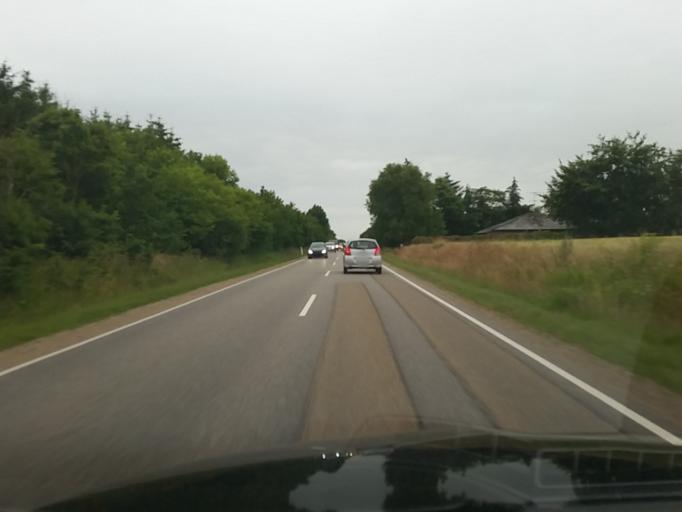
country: DK
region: South Denmark
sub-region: Billund Kommune
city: Grindsted
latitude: 55.6627
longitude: 8.7671
